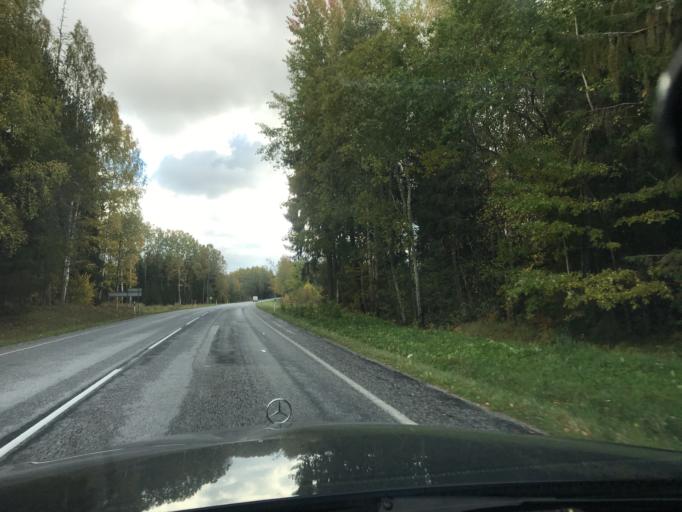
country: EE
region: Vorumaa
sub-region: Voru linn
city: Voru
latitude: 57.7269
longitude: 27.3111
